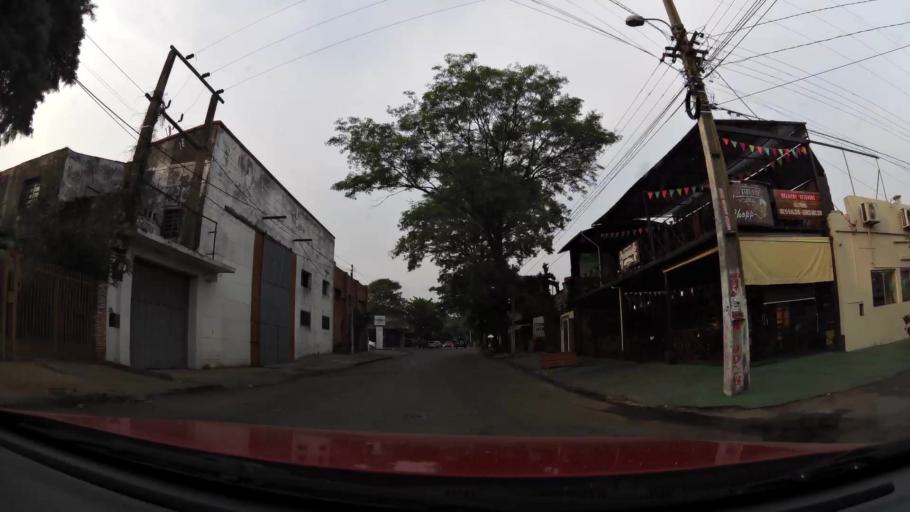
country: PY
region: Central
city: Lambare
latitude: -25.3223
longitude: -57.5738
